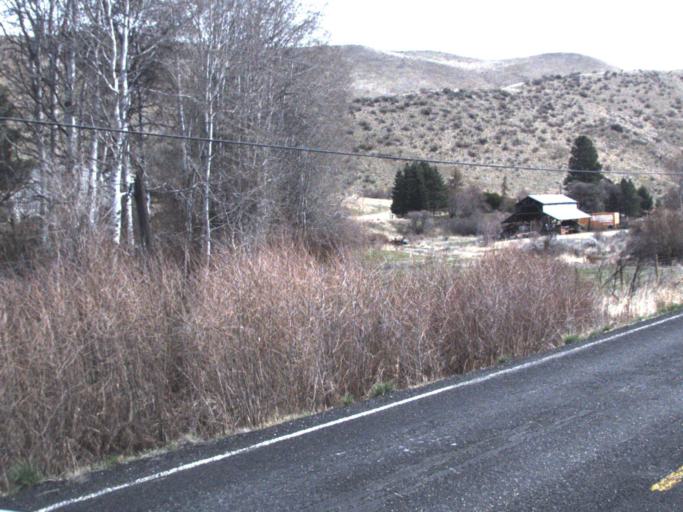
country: US
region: Washington
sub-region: Yakima County
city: Tieton
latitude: 46.7777
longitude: -120.8595
